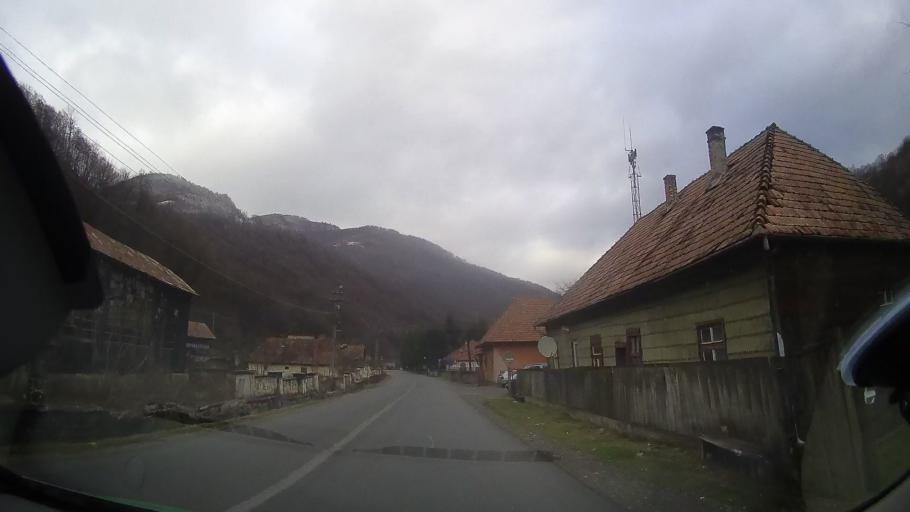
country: RO
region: Cluj
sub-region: Comuna Maguri-Racatau
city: Maguri-Racatau
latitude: 46.6473
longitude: 23.1964
